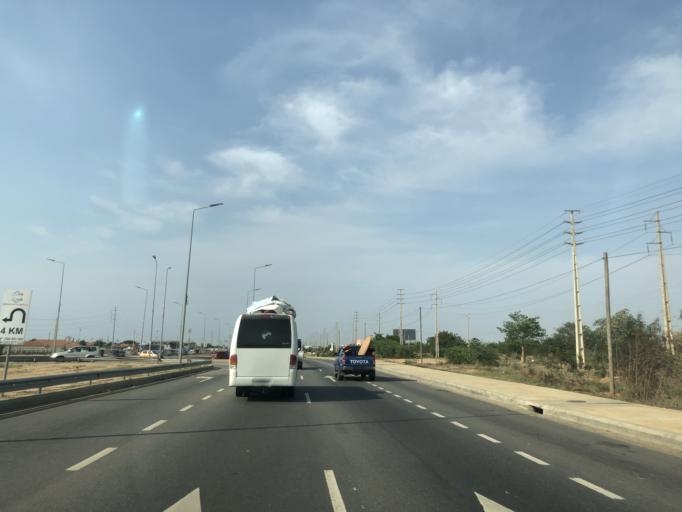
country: AO
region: Luanda
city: Luanda
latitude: -8.9484
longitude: 13.2603
